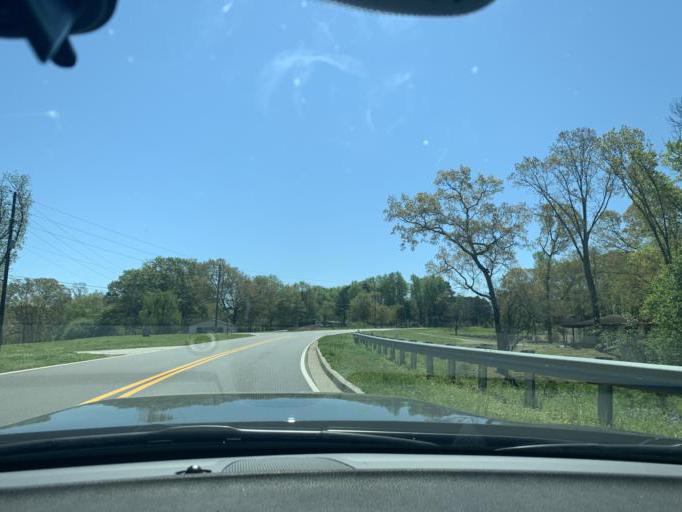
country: US
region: Georgia
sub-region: Forsyth County
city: Cumming
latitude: 34.1867
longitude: -84.1733
